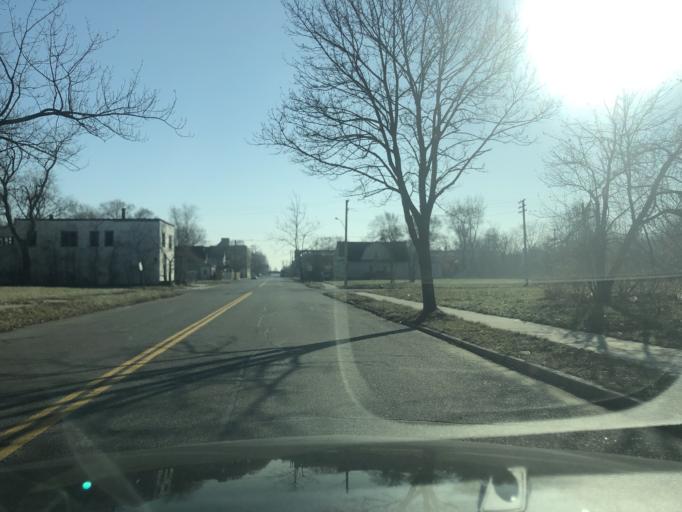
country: US
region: Michigan
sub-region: Wayne County
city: Detroit
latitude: 42.3363
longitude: -83.1049
